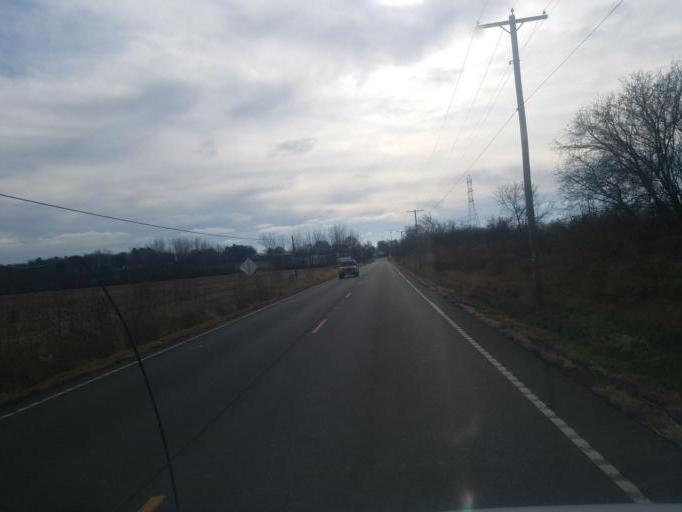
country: US
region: Ohio
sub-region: Knox County
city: Mount Vernon
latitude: 40.4172
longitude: -82.5026
